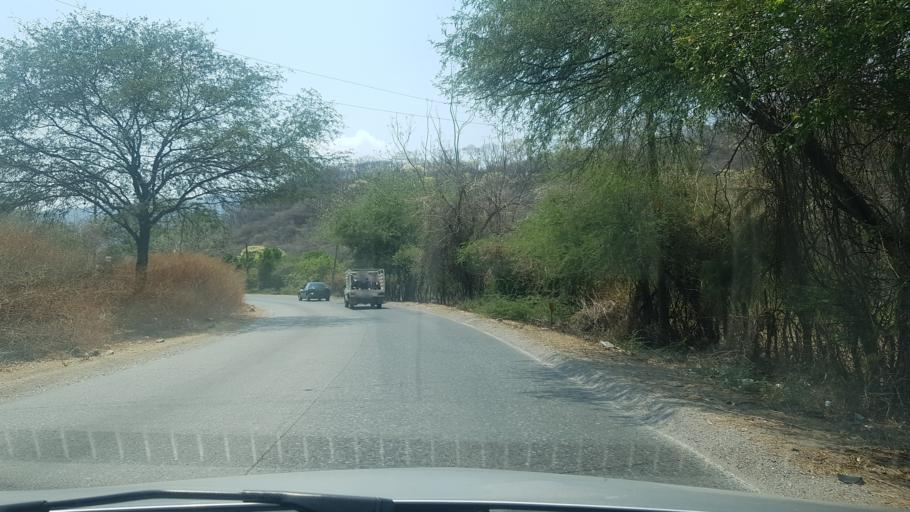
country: MX
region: Morelos
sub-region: Jiutepec
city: Independencia
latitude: 18.8026
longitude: -99.0960
